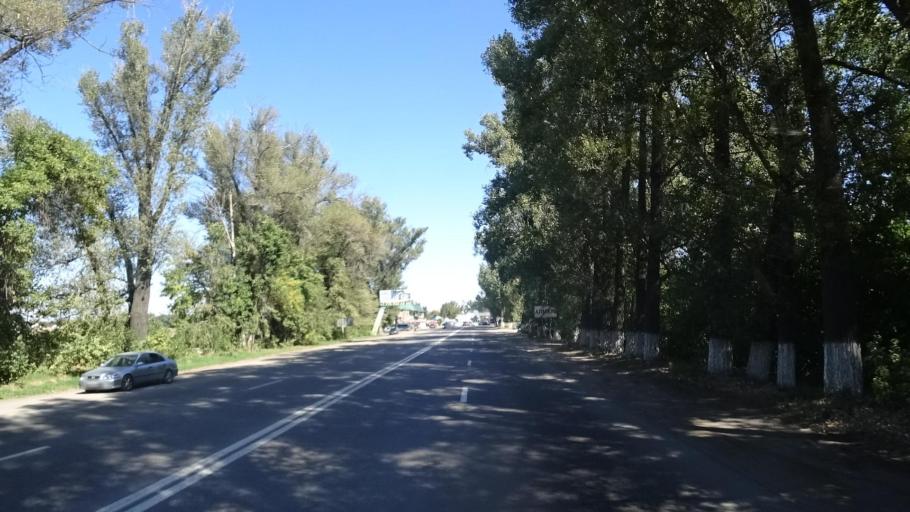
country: KZ
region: Almaty Oblysy
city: Energeticheskiy
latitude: 43.3350
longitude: 77.0387
